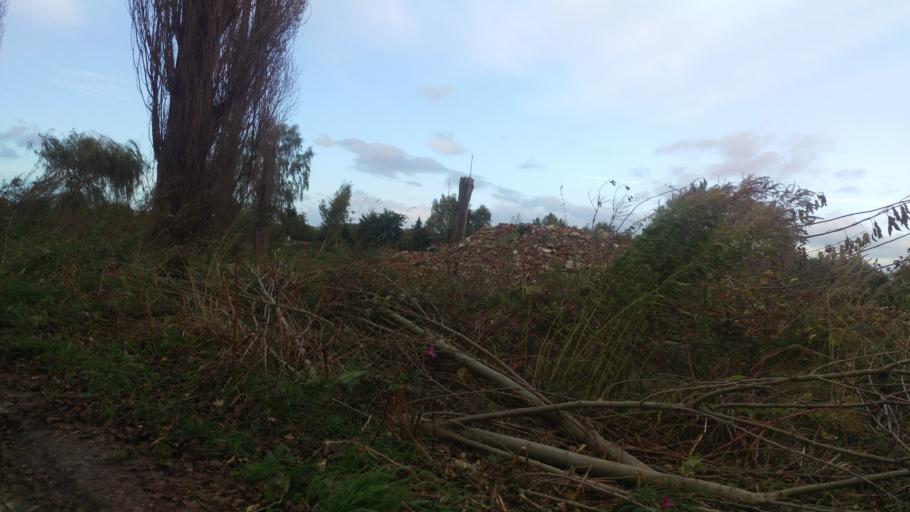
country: PL
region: West Pomeranian Voivodeship
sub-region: Szczecin
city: Szczecin
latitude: 53.4021
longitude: 14.6683
